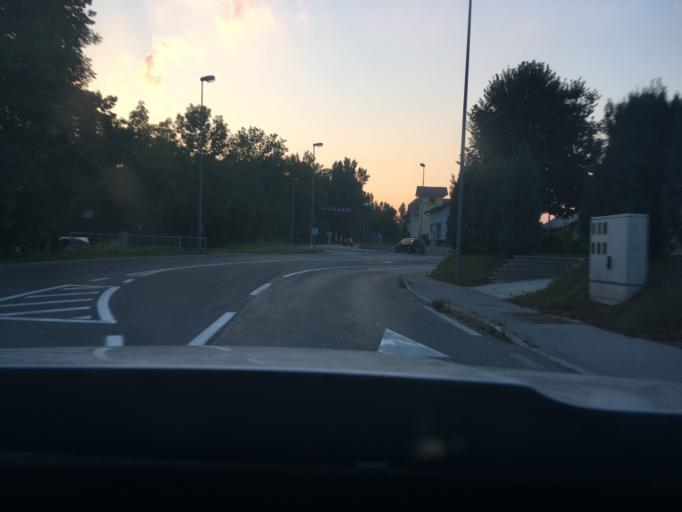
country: SI
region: Ribnica
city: Ribnica
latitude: 45.7339
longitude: 14.7331
